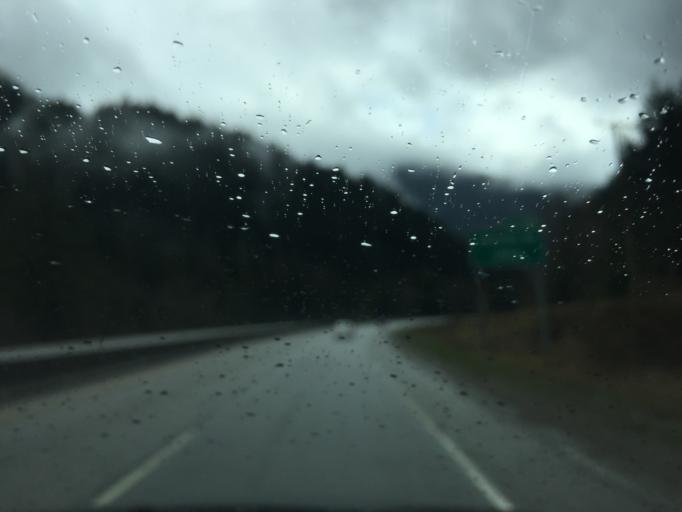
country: CA
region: British Columbia
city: Hope
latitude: 49.4038
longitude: -121.3161
